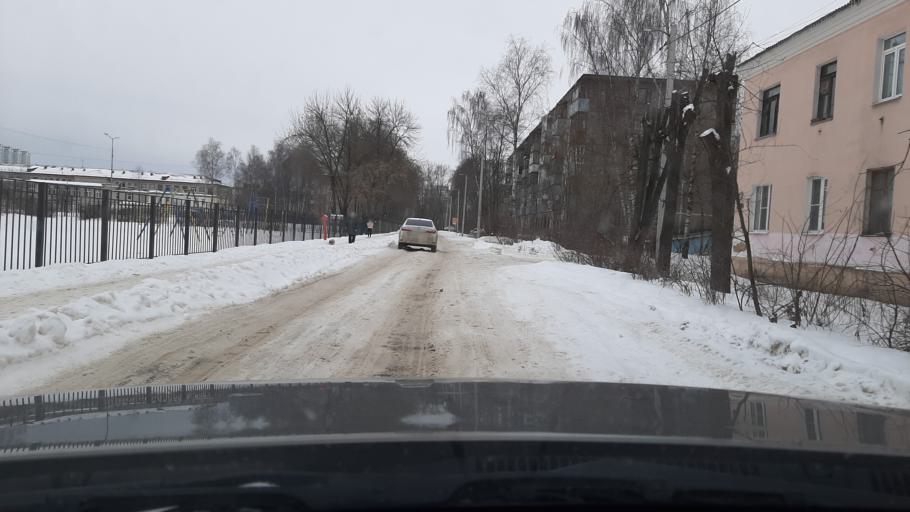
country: RU
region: Ivanovo
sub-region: Gorod Ivanovo
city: Ivanovo
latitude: 56.9689
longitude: 40.9673
